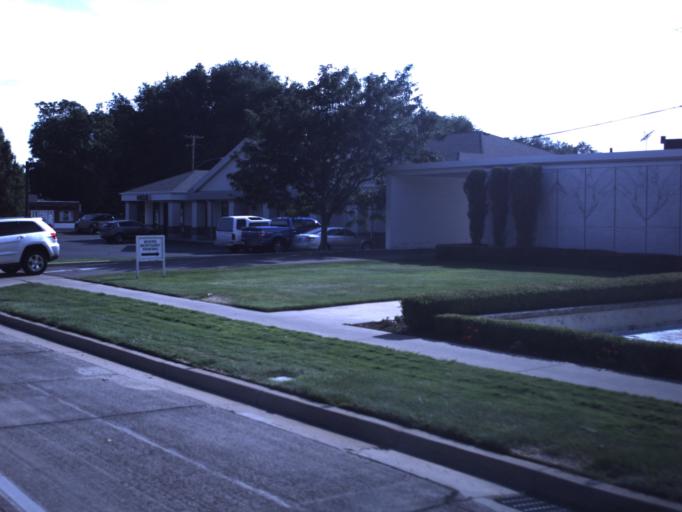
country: US
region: Utah
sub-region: Weber County
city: Ogden
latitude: 41.2494
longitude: -111.9700
